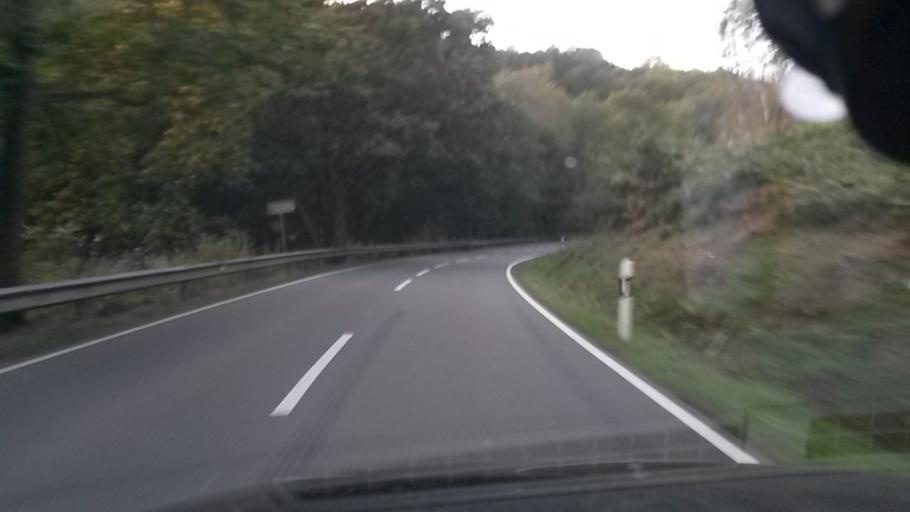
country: DE
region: North Rhine-Westphalia
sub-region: Regierungsbezirk Koln
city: Engelskirchen
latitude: 51.0204
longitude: 7.4391
